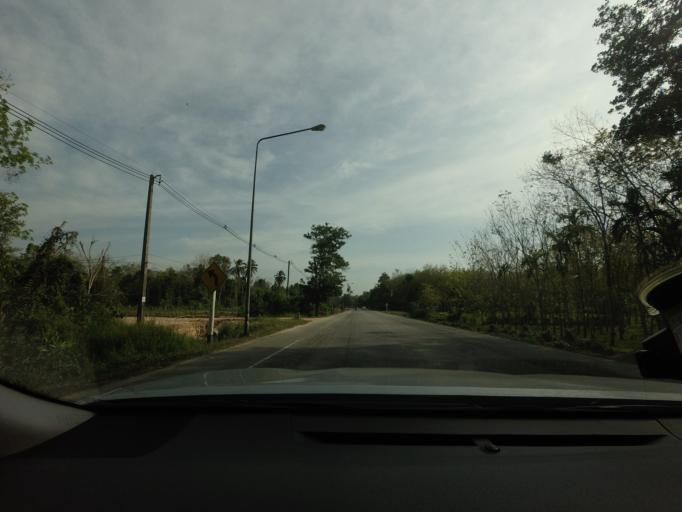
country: TH
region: Narathiwat
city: Narathiwat
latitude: 6.3581
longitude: 101.7911
